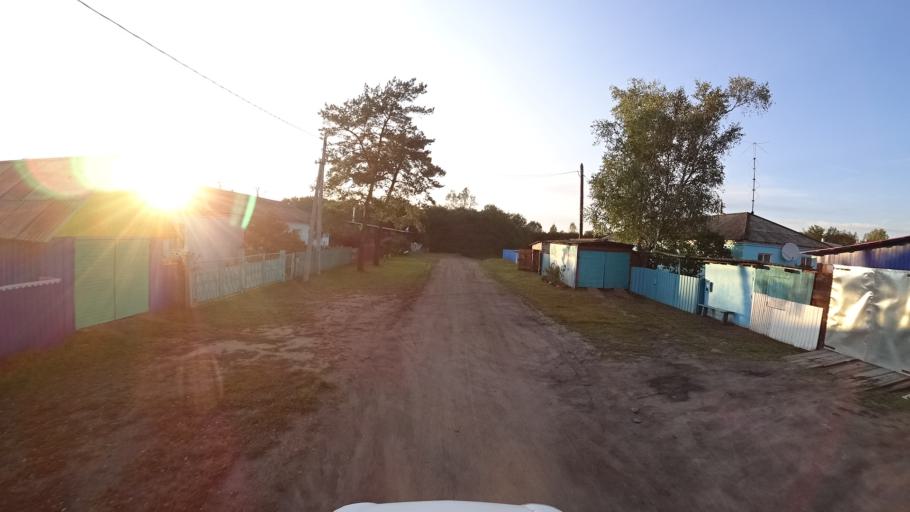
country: RU
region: Amur
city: Arkhara
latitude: 49.3612
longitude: 130.1138
